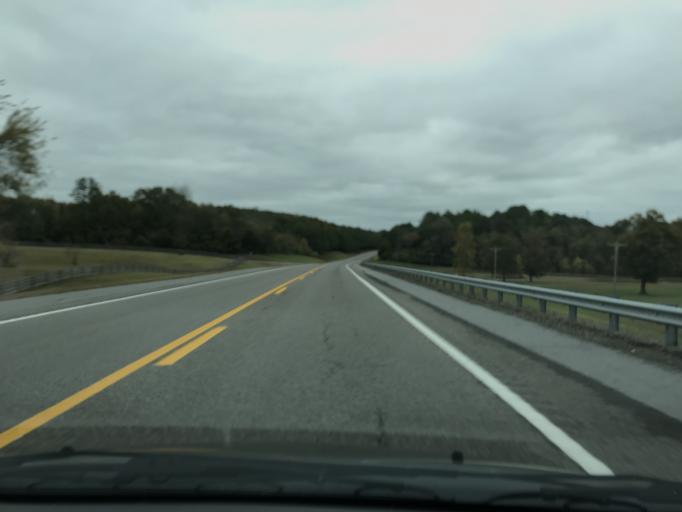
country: US
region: Tennessee
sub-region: Rhea County
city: Dayton
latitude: 35.4359
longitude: -85.0237
